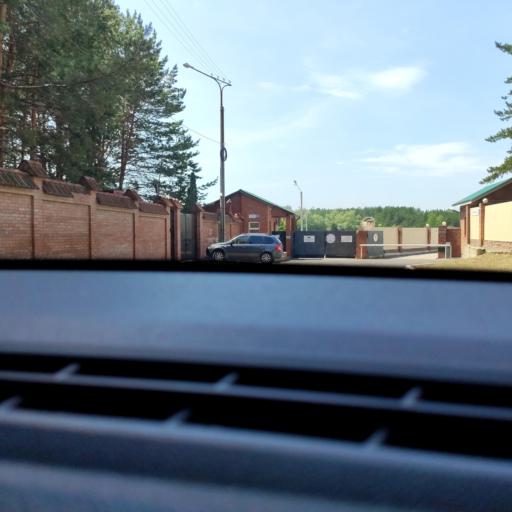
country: RU
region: Samara
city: Tol'yatti
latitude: 53.4759
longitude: 49.3168
